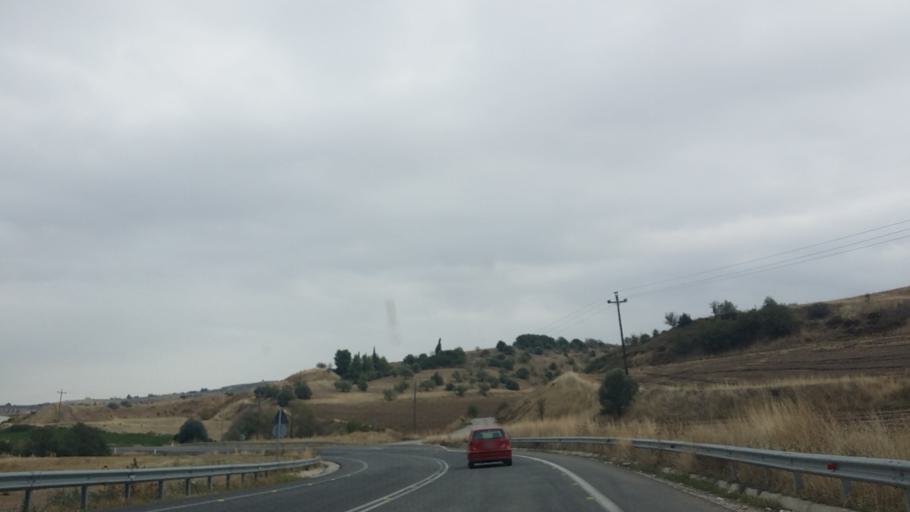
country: GR
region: Central Greece
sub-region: Nomos Voiotias
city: Vagia
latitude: 38.3019
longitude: 23.2352
